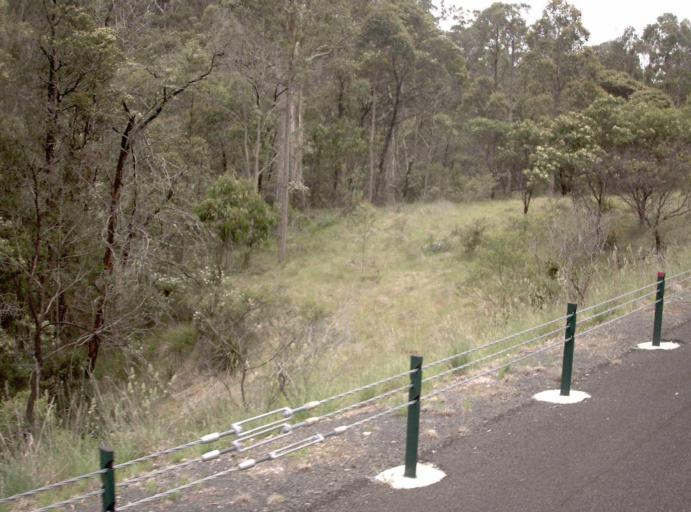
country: AU
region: New South Wales
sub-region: Bombala
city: Bombala
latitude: -37.2521
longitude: 149.2486
